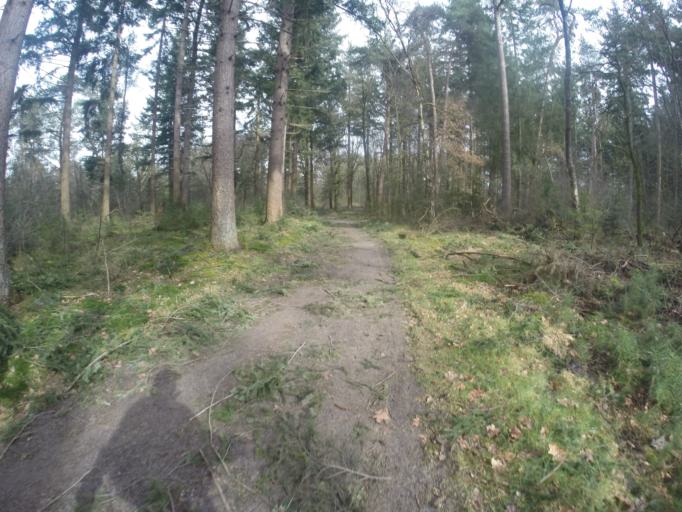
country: NL
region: Gelderland
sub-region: Gemeente Bronckhorst
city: Zelhem
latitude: 52.0360
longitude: 6.3827
